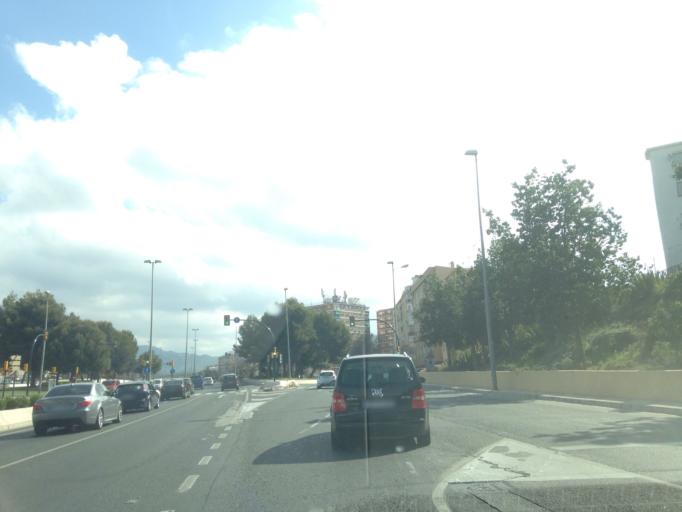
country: ES
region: Andalusia
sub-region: Provincia de Malaga
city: Malaga
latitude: 36.7284
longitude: -4.4458
